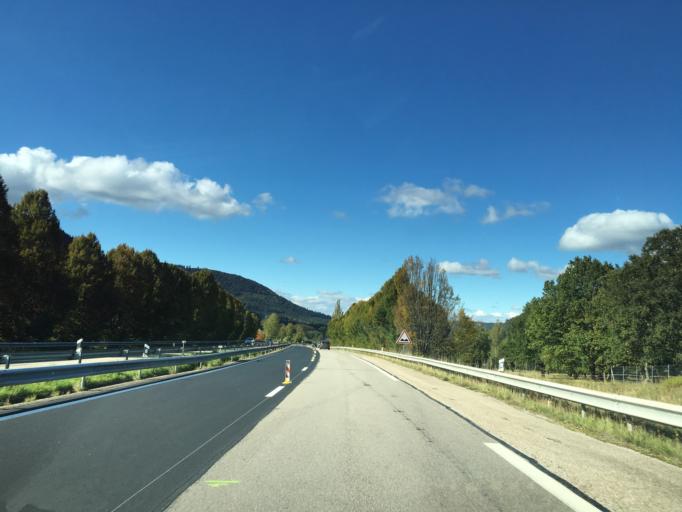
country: FR
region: Lorraine
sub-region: Departement des Vosges
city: Etival-Clairefontaine
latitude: 48.3725
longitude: 6.8801
